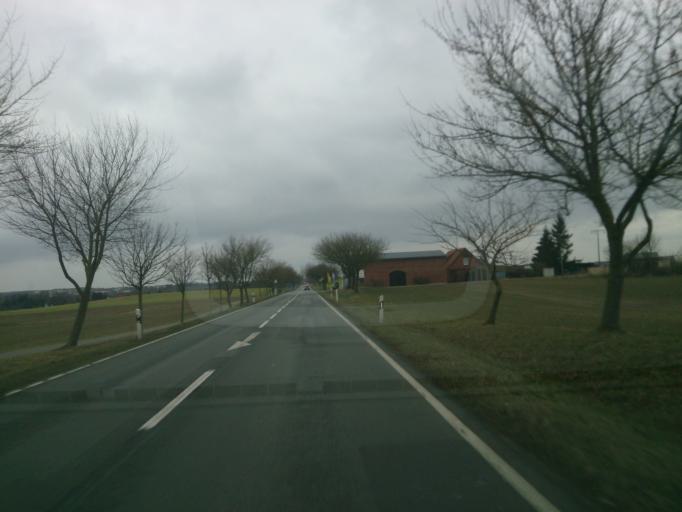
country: DE
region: Mecklenburg-Vorpommern
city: Wackerow
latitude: 53.6785
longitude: 12.9070
